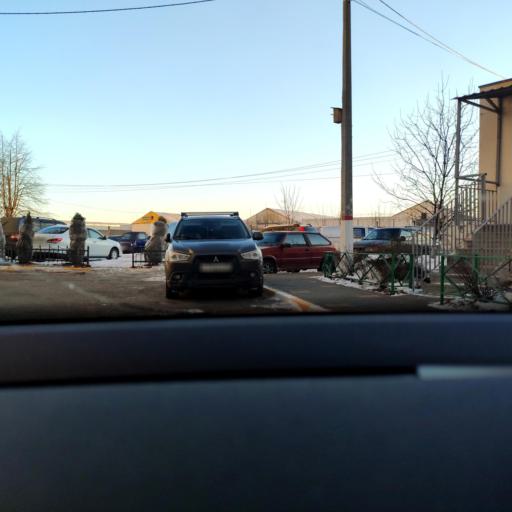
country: RU
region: Moskovskaya
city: Oktyabr'skiy
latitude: 55.5960
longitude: 37.9851
